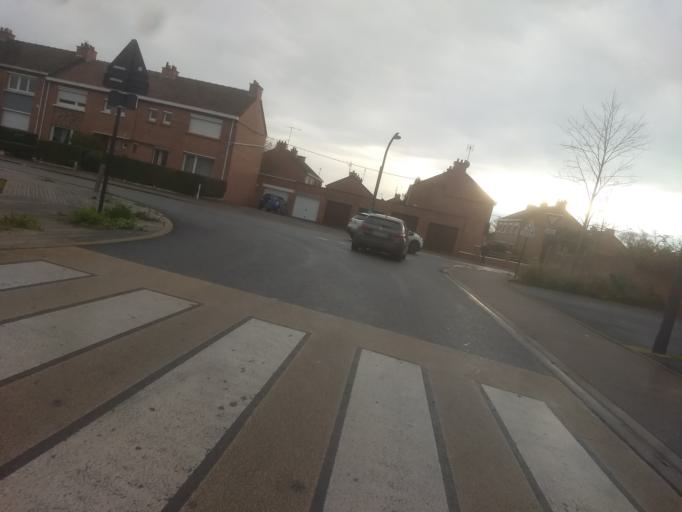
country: FR
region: Nord-Pas-de-Calais
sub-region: Departement du Pas-de-Calais
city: Dainville
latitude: 50.2884
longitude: 2.7377
